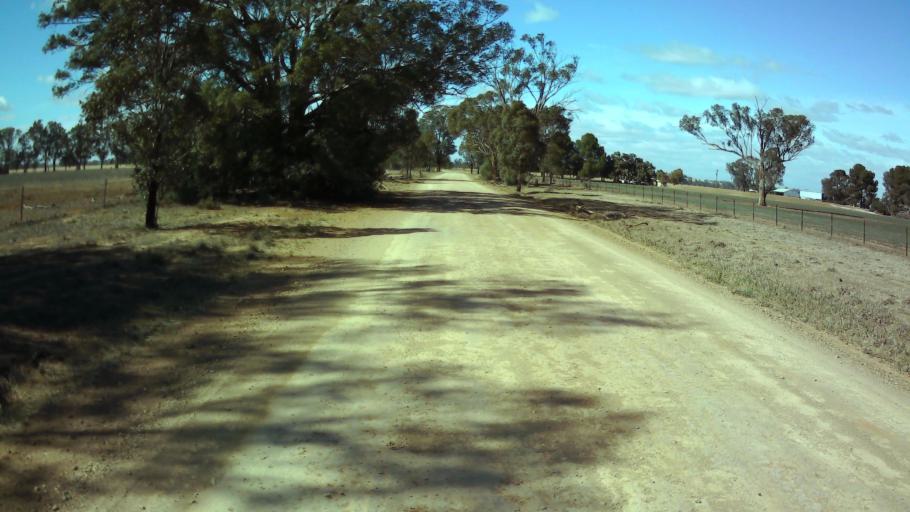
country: AU
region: New South Wales
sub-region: Weddin
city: Grenfell
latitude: -34.0272
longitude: 148.3179
